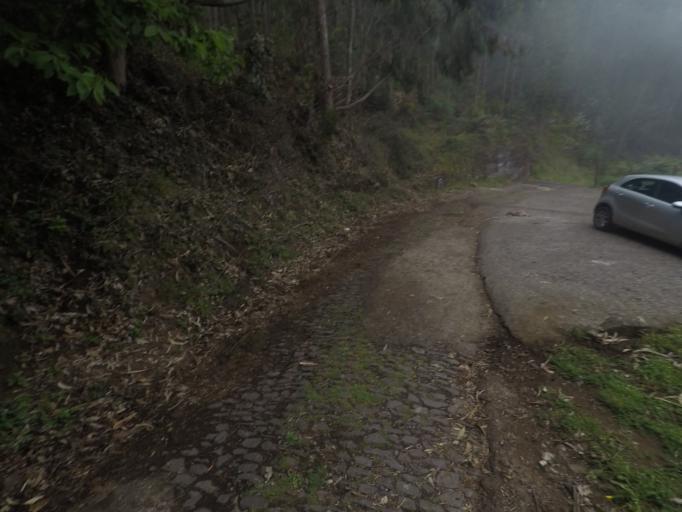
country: PT
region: Madeira
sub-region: Calheta
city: Arco da Calheta
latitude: 32.7296
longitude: -17.0959
